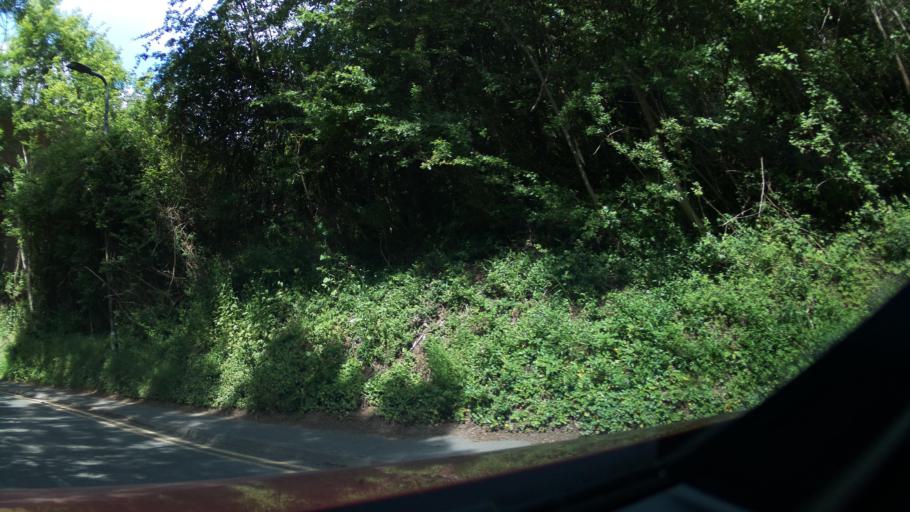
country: GB
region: England
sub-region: Herefordshire
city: Ross on Wye
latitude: 51.9211
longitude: -2.5887
